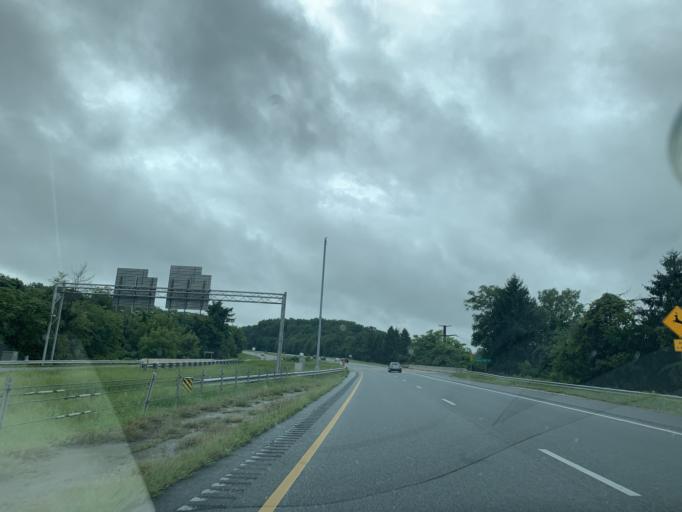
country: US
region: Maryland
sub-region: Baltimore County
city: Reisterstown
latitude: 39.4650
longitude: -76.8378
